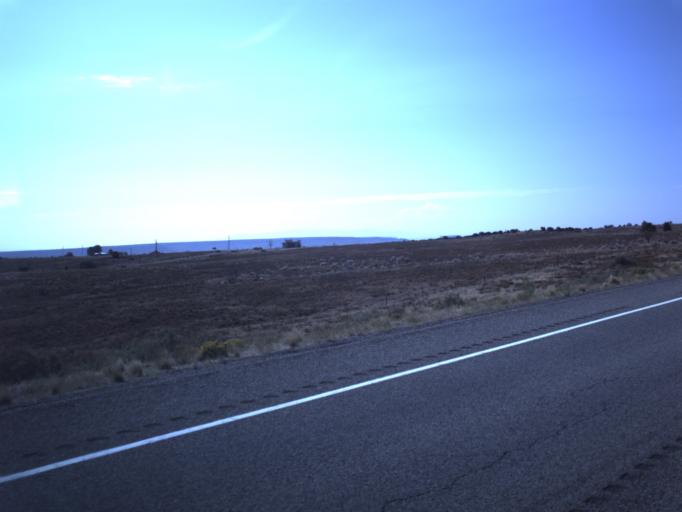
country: US
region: Utah
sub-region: San Juan County
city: Blanding
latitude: 37.4420
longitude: -109.4685
